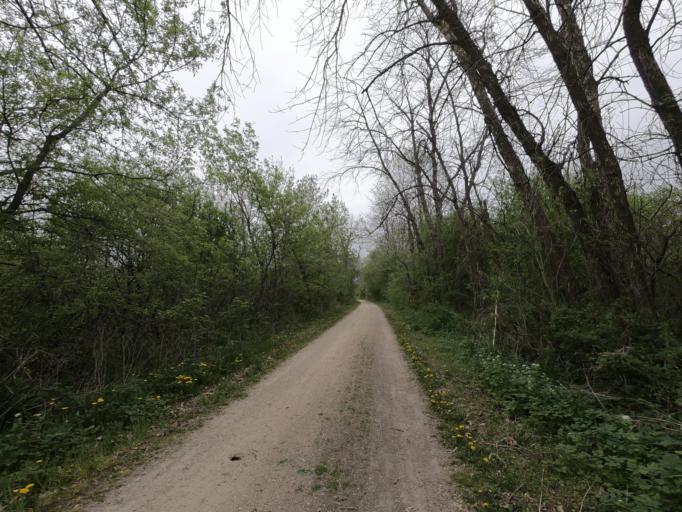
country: US
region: Wisconsin
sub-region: Jefferson County
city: Jefferson
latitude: 43.0375
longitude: -88.8289
